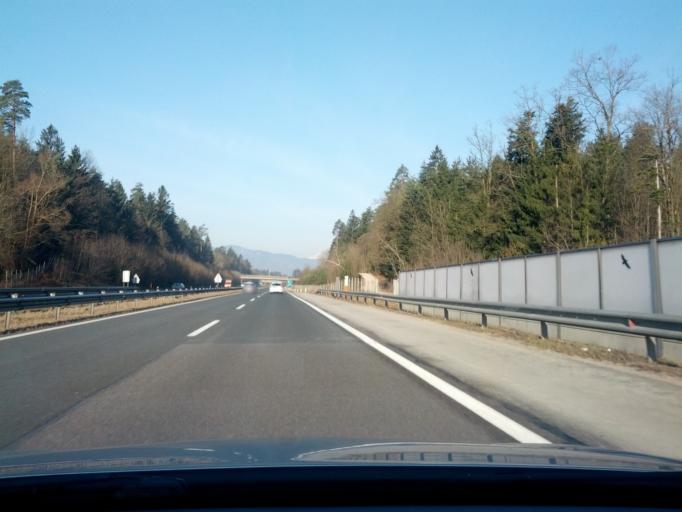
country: SI
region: Kranj
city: Kokrica
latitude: 46.2603
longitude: 14.3671
